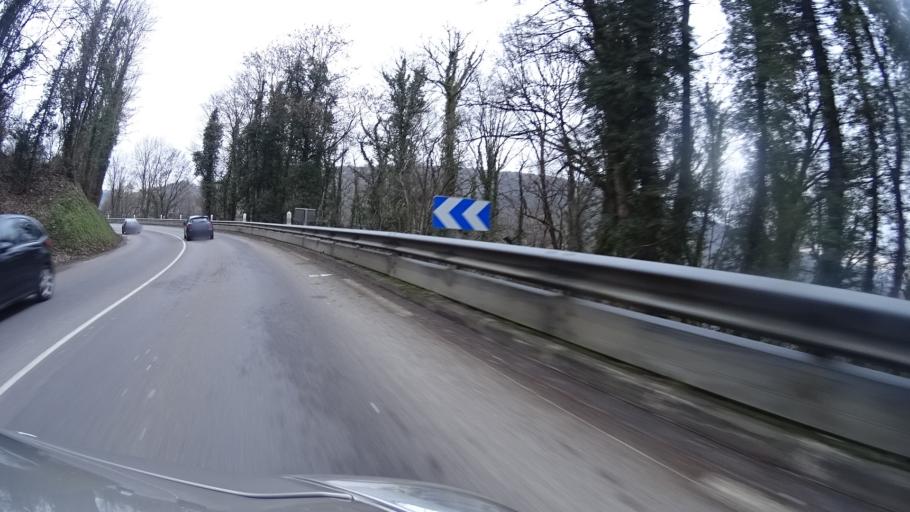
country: FR
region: Franche-Comte
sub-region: Departement du Doubs
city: Morre
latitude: 47.2302
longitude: 6.0616
